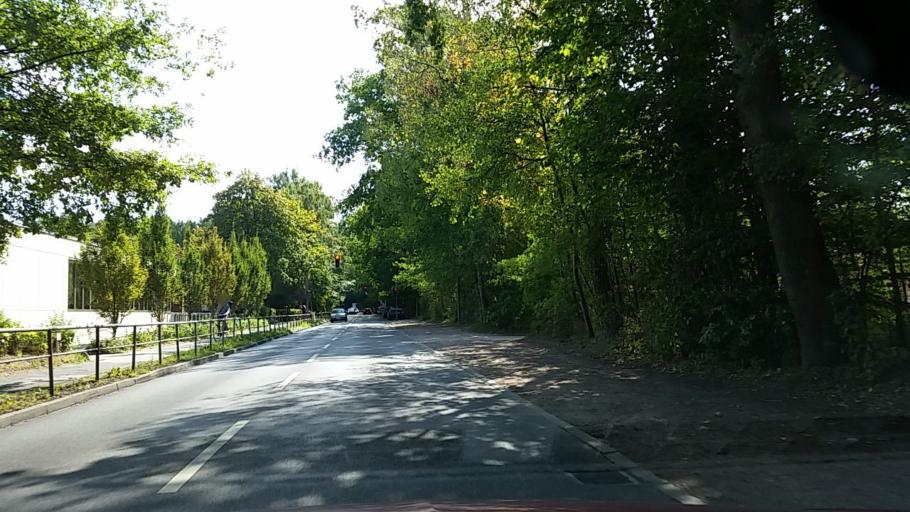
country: DE
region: Hamburg
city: Bergstedt
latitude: 53.6657
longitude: 10.1479
